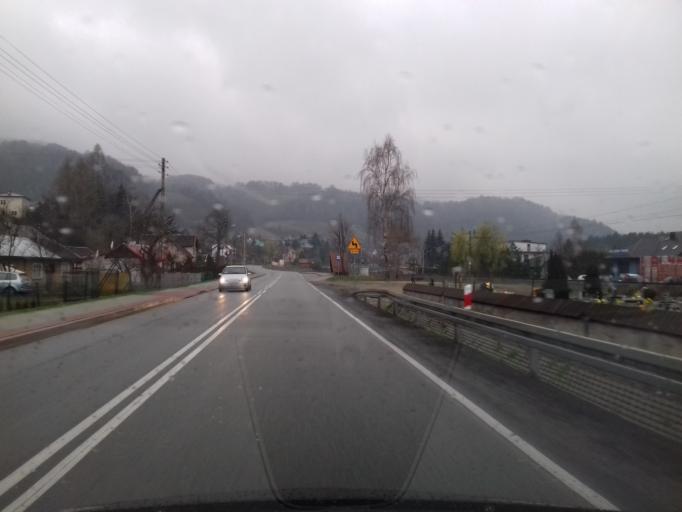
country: PL
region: Lesser Poland Voivodeship
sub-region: Powiat nowosadecki
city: Piwniczna-Zdroj
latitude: 49.4494
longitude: 20.7022
